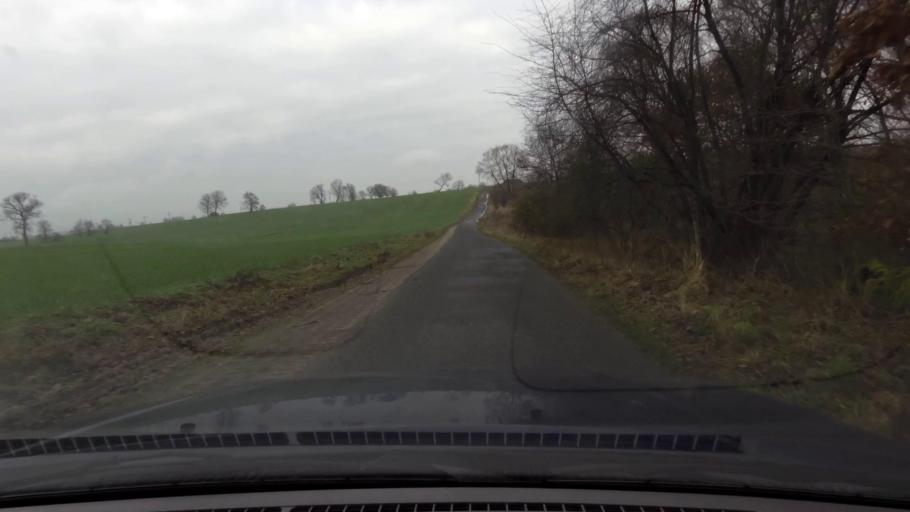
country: PL
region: West Pomeranian Voivodeship
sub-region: Powiat stargardzki
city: Stara Dabrowa
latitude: 53.3473
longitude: 15.1267
